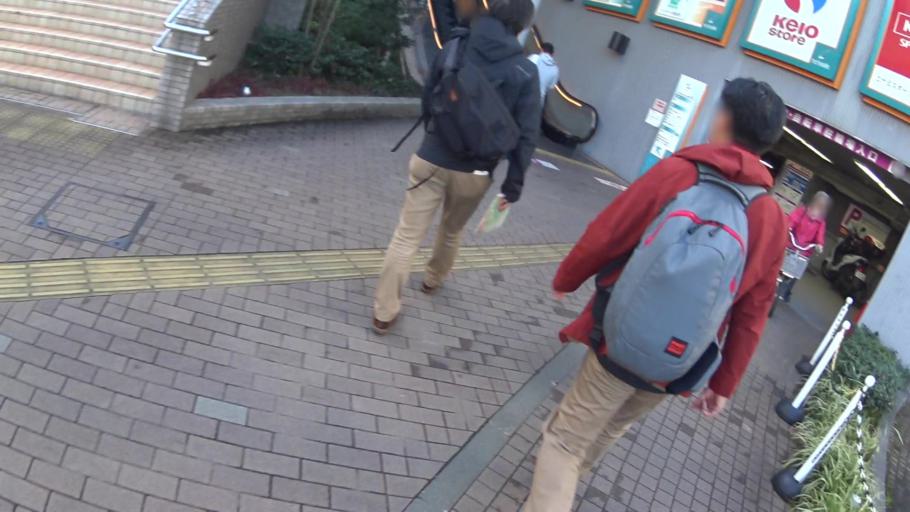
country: JP
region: Tokyo
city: Chofugaoka
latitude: 35.6366
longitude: 139.4995
